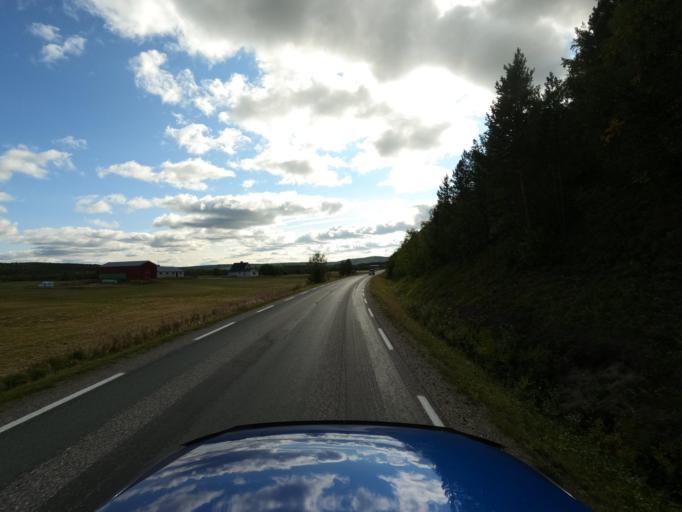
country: NO
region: Finnmark Fylke
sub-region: Karasjok
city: Karasjohka
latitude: 69.4118
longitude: 25.8042
